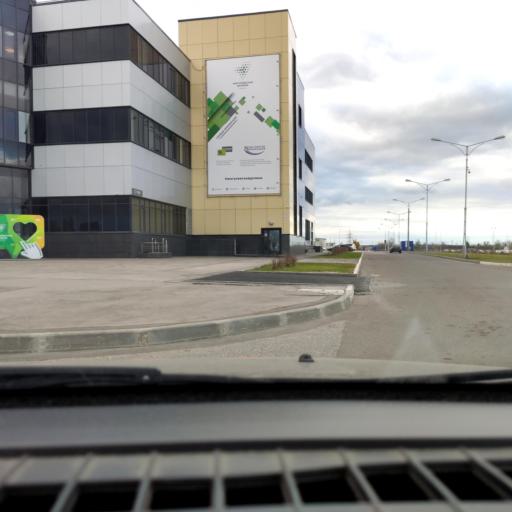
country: RU
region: Samara
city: Podstepki
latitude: 53.5573
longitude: 49.2146
